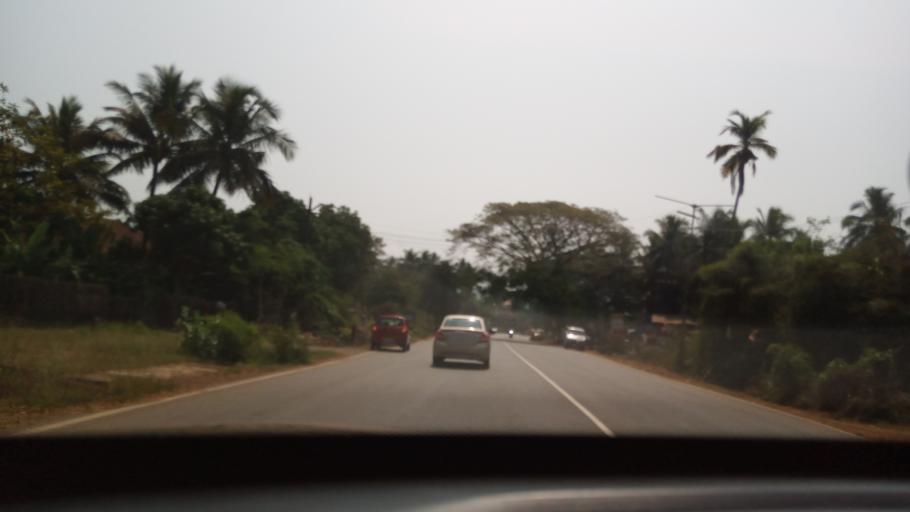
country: IN
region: Goa
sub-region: South Goa
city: Raia
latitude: 15.3228
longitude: 73.9395
